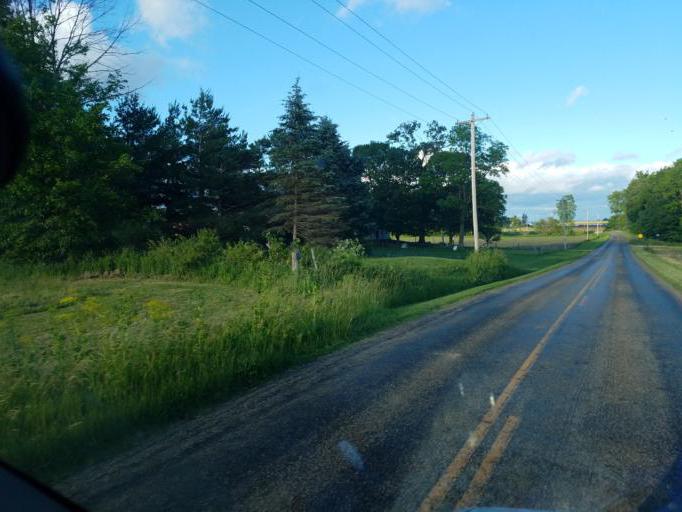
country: US
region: Ohio
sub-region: Knox County
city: Fredericktown
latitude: 40.4415
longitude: -82.6094
